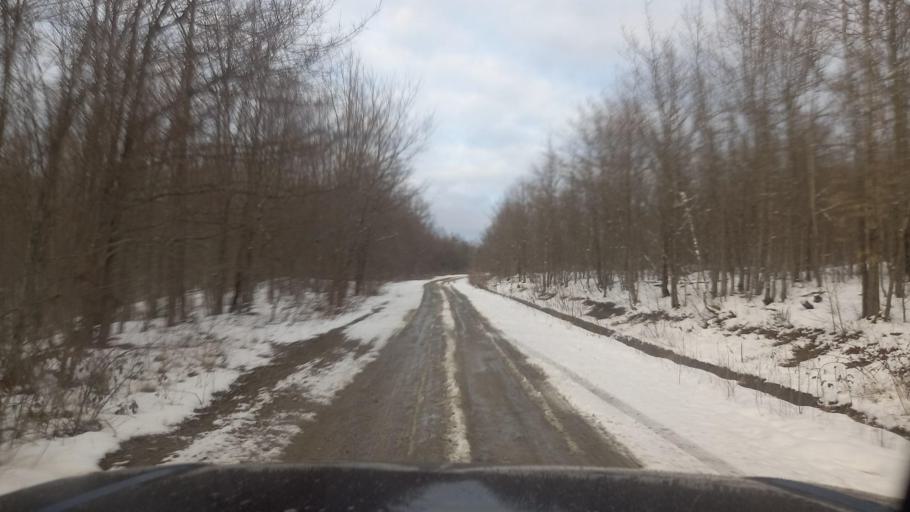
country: RU
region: Krasnodarskiy
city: Smolenskaya
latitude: 44.6778
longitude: 38.7656
